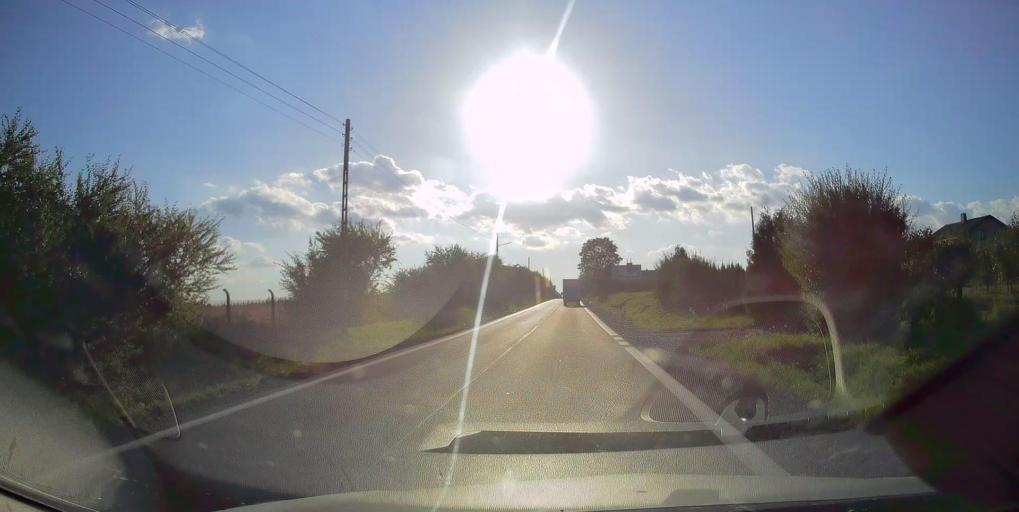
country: PL
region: Lodz Voivodeship
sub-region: Powiat rawski
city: Biala Rawska
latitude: 51.8080
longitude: 20.4908
